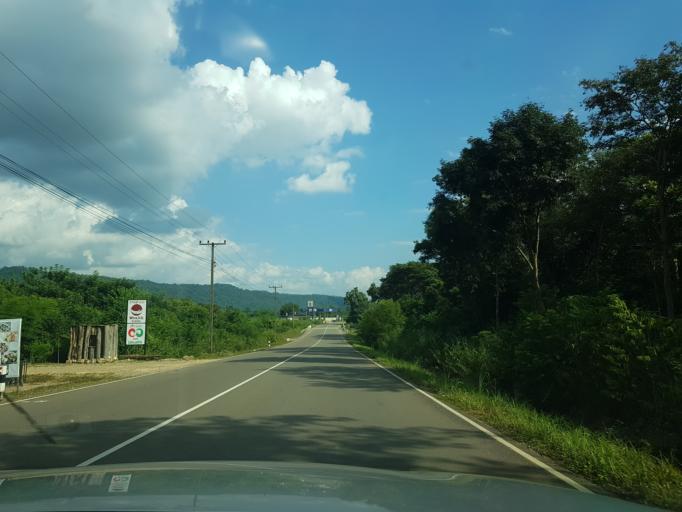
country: TH
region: Nong Khai
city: Sangkhom
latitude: 18.0313
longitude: 102.3725
